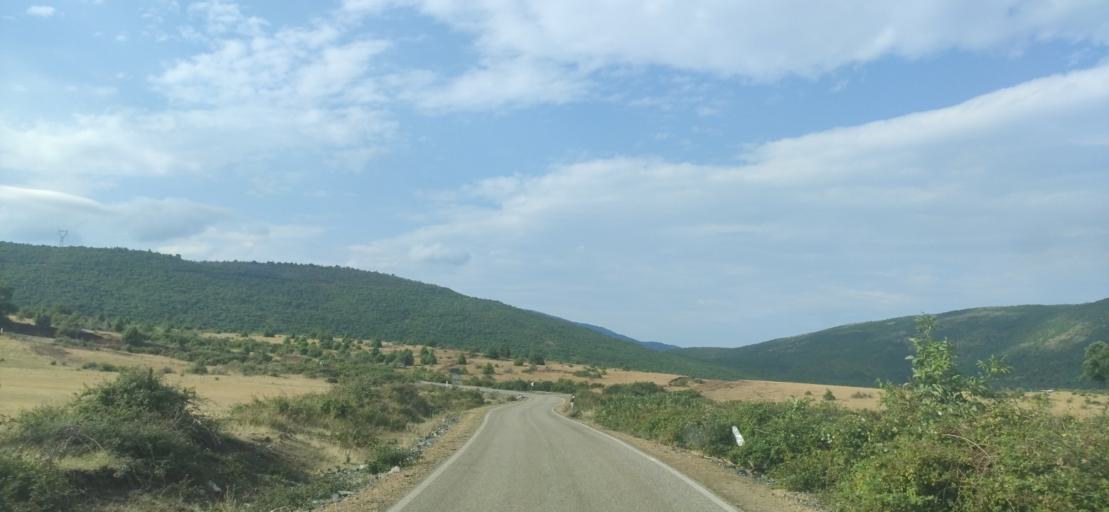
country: AL
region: Shkoder
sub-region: Rrethi i Pukes
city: Iballe
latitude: 42.1843
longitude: 19.9941
